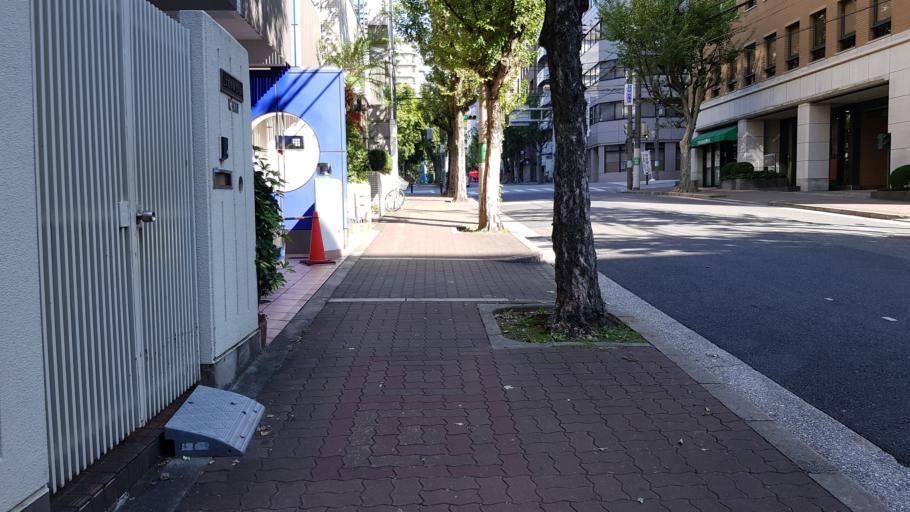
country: JP
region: Osaka
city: Osaka-shi
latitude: 34.6888
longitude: 135.5140
